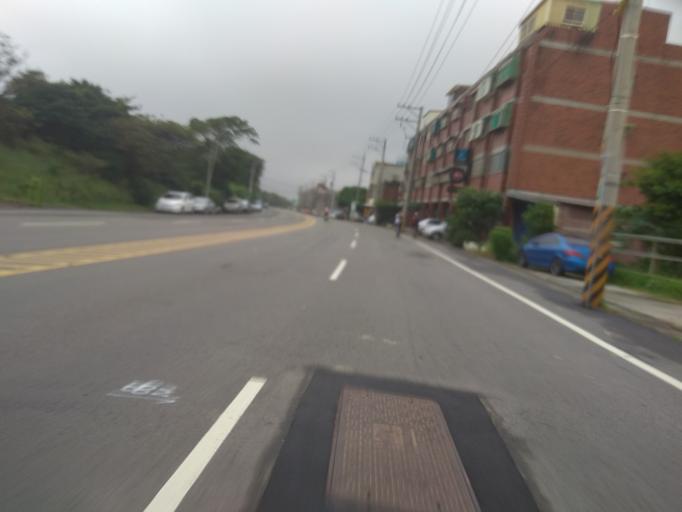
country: TW
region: Taiwan
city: Taoyuan City
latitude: 25.0316
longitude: 121.1020
